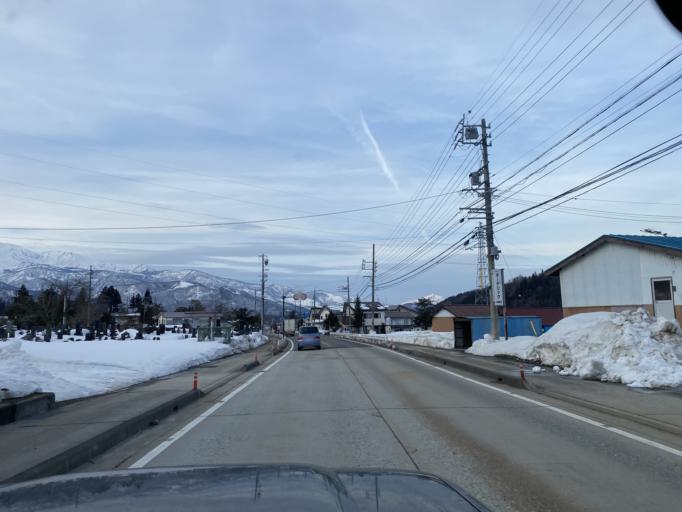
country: JP
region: Nagano
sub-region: Kitaazumi Gun
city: Hakuba
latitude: 36.6610
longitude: 137.8488
